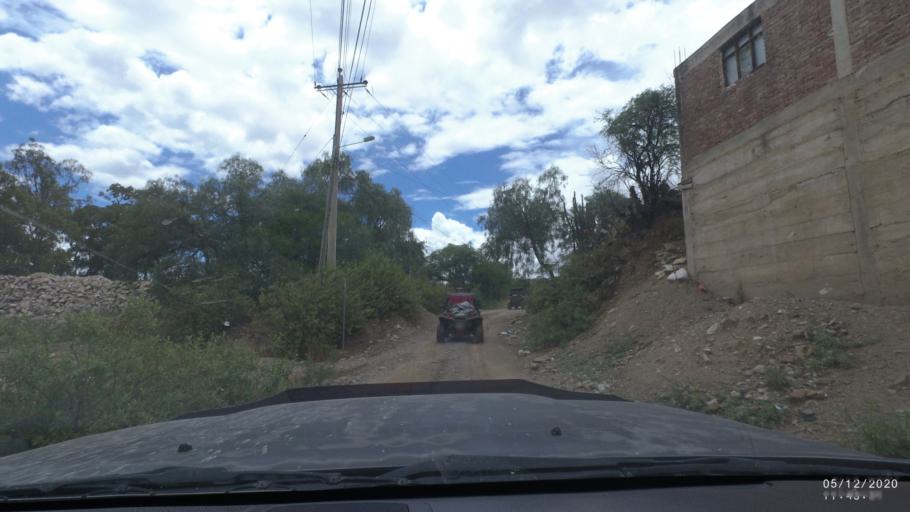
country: BO
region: Cochabamba
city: Sipe Sipe
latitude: -17.5573
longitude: -66.3414
